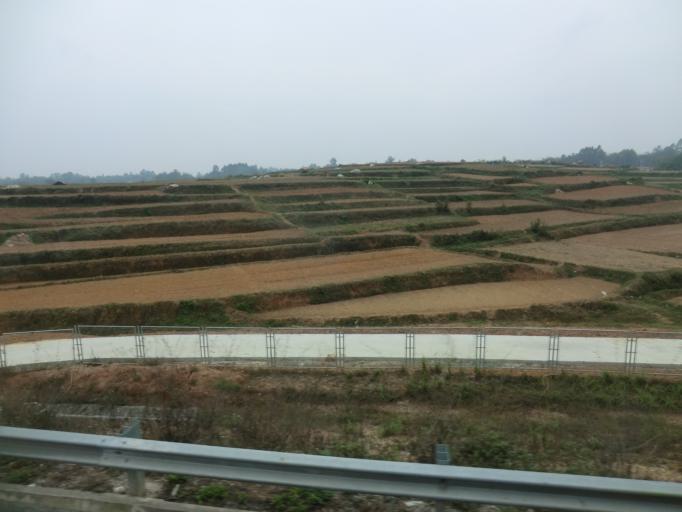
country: VN
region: Phu Tho
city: Viet Tri
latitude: 21.3609
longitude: 105.4285
